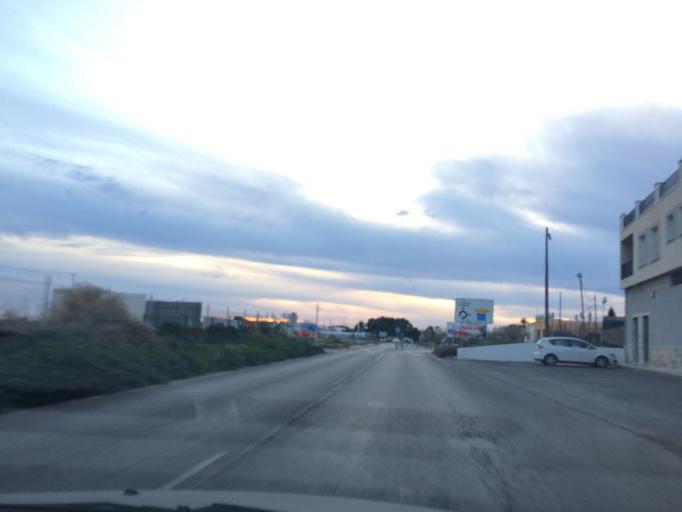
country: ES
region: Andalusia
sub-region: Provincia de Almeria
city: Viator
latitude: 36.8421
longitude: -2.3971
